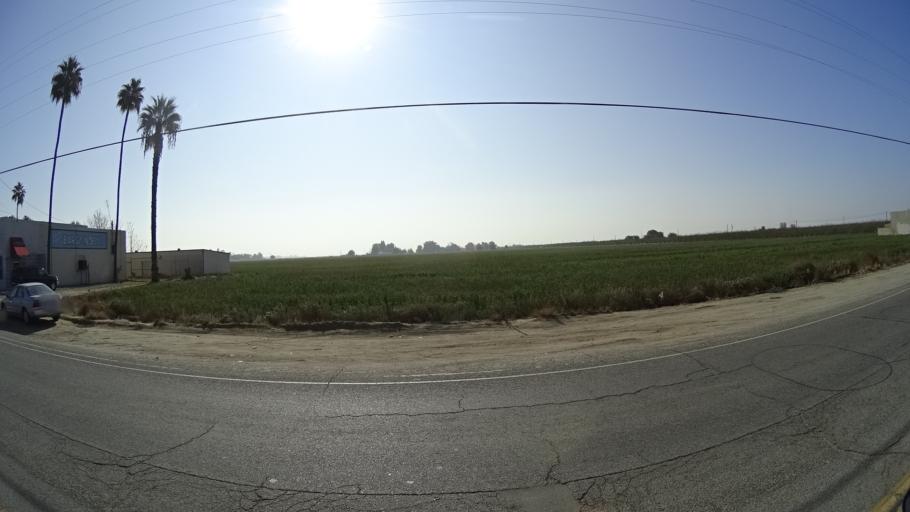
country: US
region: California
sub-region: Kern County
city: Greenfield
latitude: 35.2668
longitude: -119.0375
